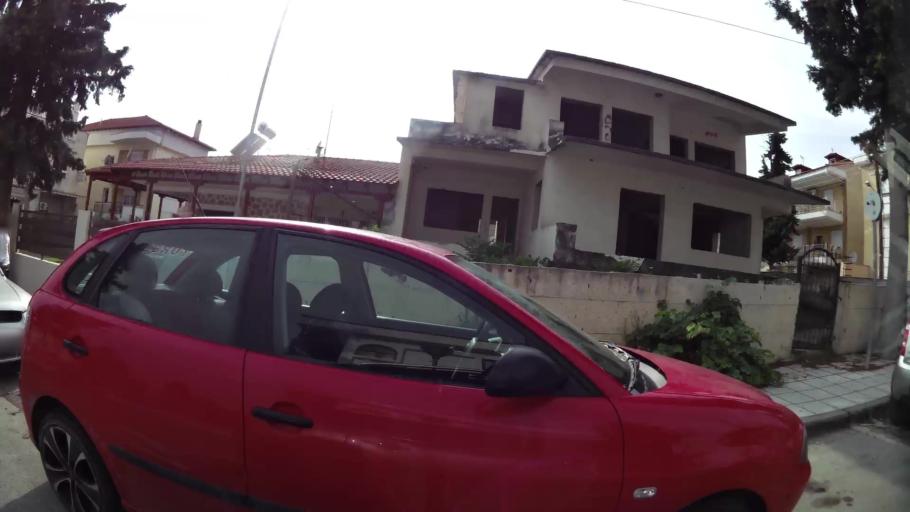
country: GR
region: Central Macedonia
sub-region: Nomos Thessalonikis
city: Oraiokastro
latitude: 40.7319
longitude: 22.9178
